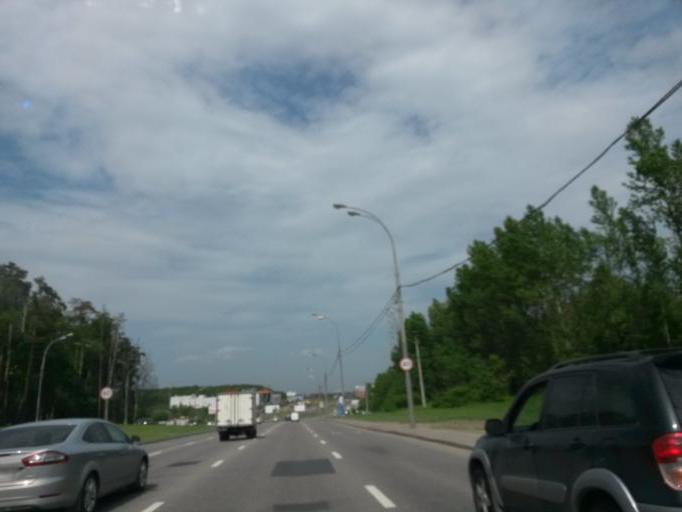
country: RU
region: Moscow
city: Chertanovo Yuzhnoye
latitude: 55.5595
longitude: 37.5549
